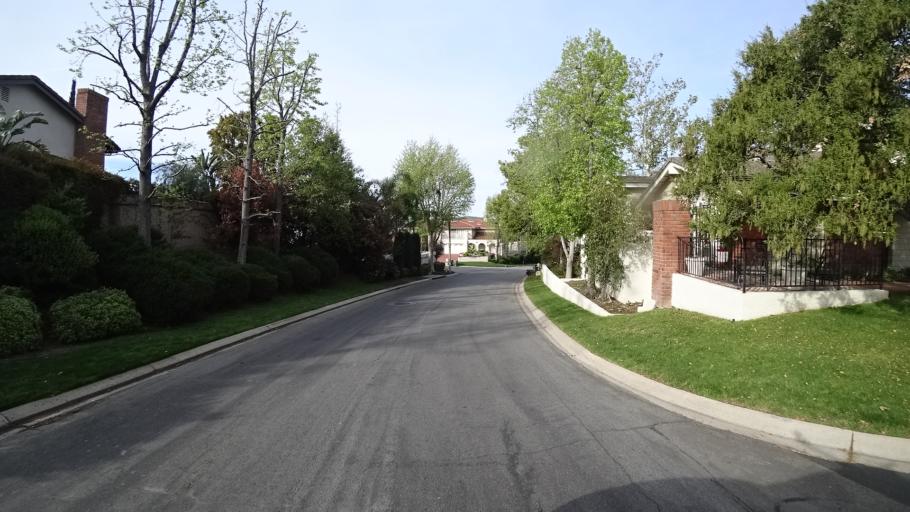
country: US
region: California
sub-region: Ventura County
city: Thousand Oaks
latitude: 34.1946
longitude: -118.8103
